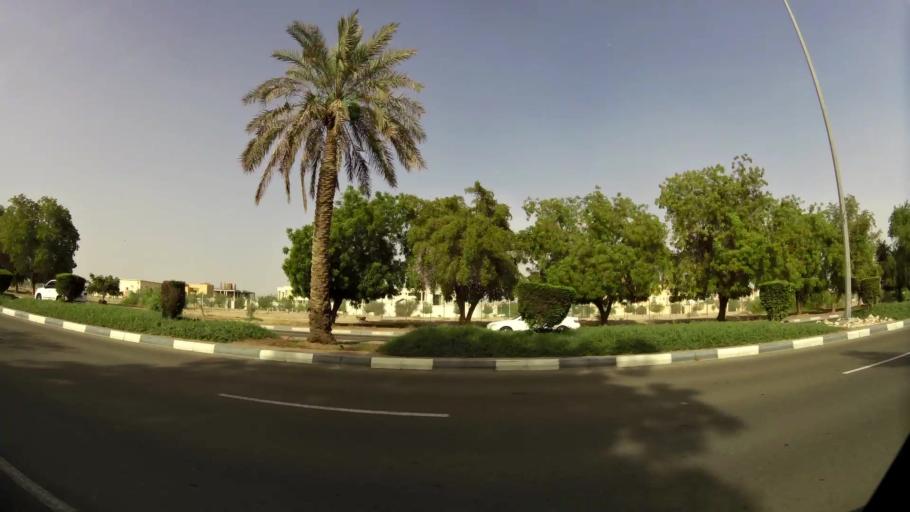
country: AE
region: Abu Dhabi
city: Al Ain
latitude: 24.1630
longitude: 55.7116
